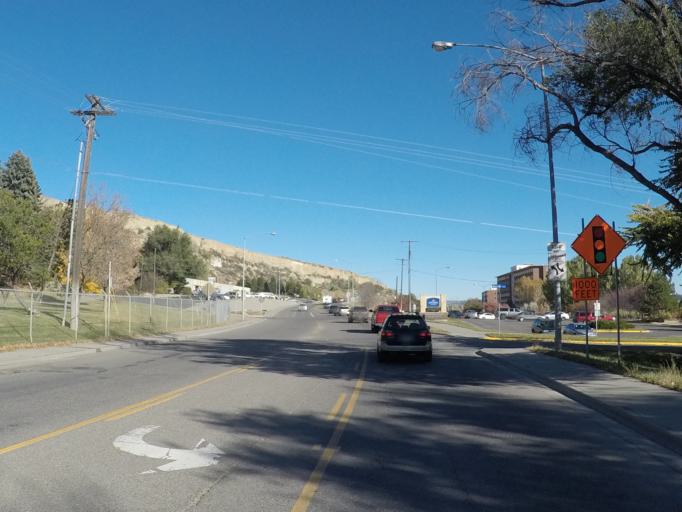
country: US
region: Montana
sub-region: Yellowstone County
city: Billings
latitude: 45.7983
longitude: -108.5256
